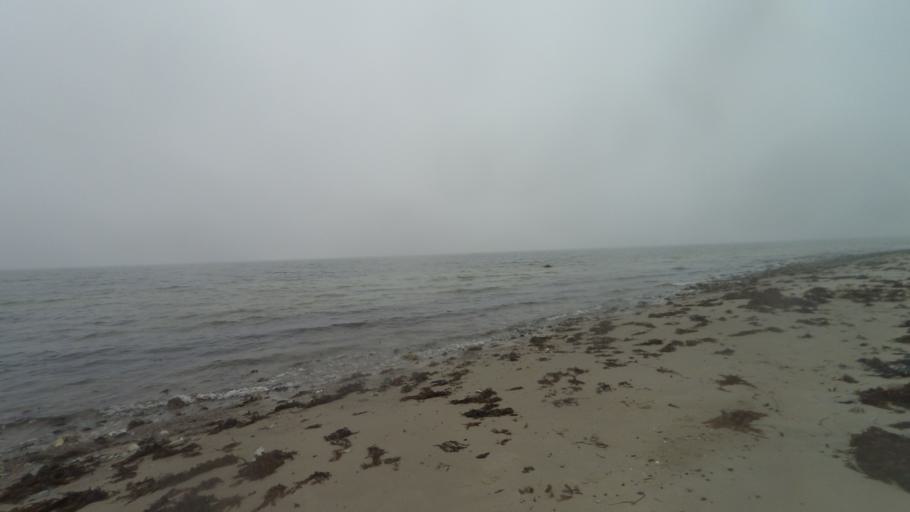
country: DK
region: Central Jutland
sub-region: Odder Kommune
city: Odder
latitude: 55.9370
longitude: 10.2603
